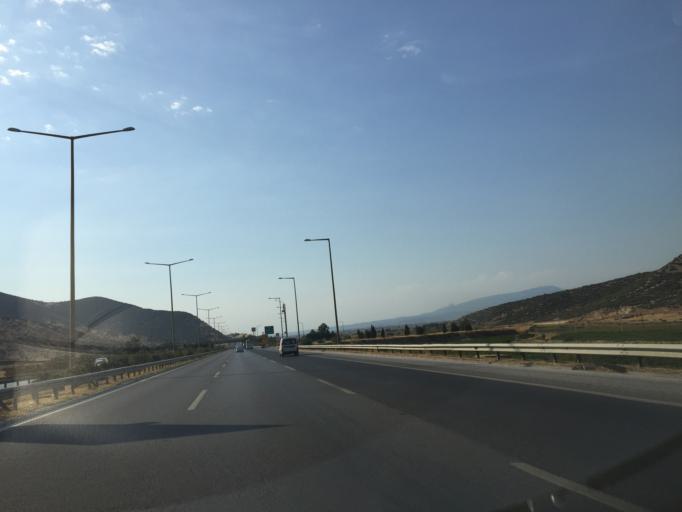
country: TR
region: Izmir
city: Belevi
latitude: 38.0649
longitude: 27.4164
